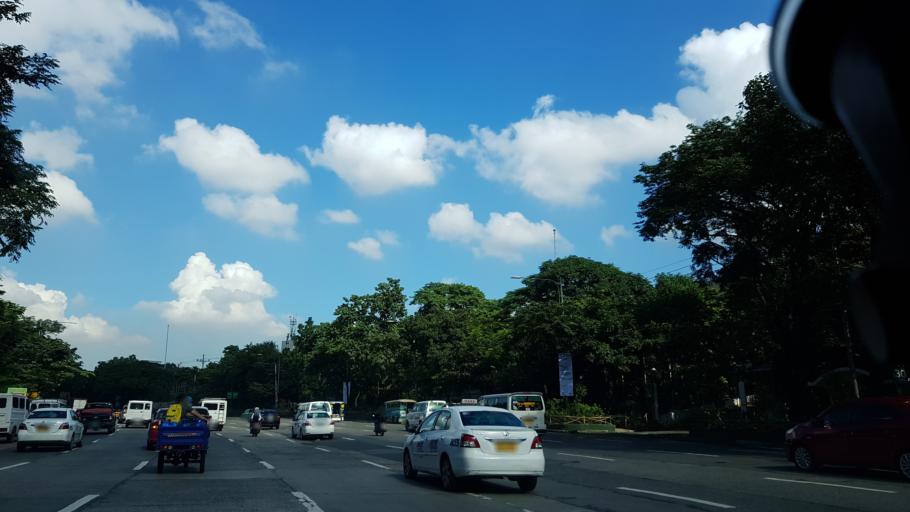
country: PH
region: Metro Manila
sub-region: Quezon City
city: Quezon City
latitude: 14.6538
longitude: 121.0505
